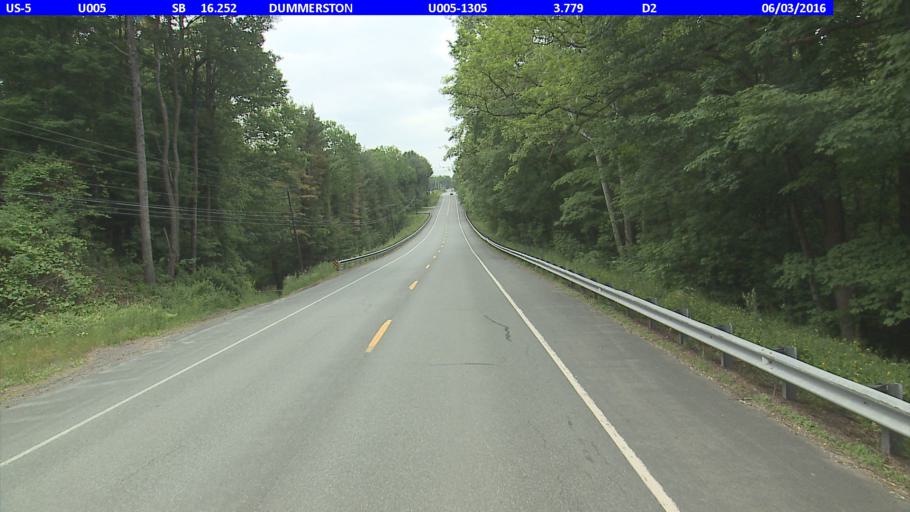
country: US
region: New Hampshire
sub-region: Cheshire County
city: Chesterfield
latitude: 42.9471
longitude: -72.5362
